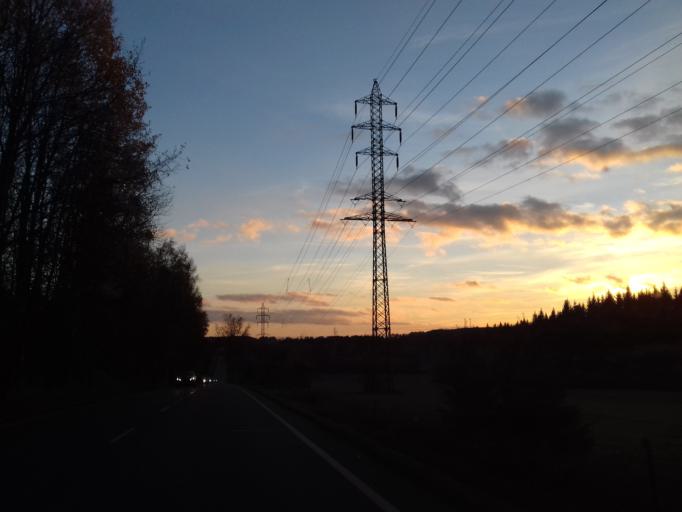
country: CZ
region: Pardubicky
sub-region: Okres Chrudim
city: Hlinsko
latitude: 49.7314
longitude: 15.8724
